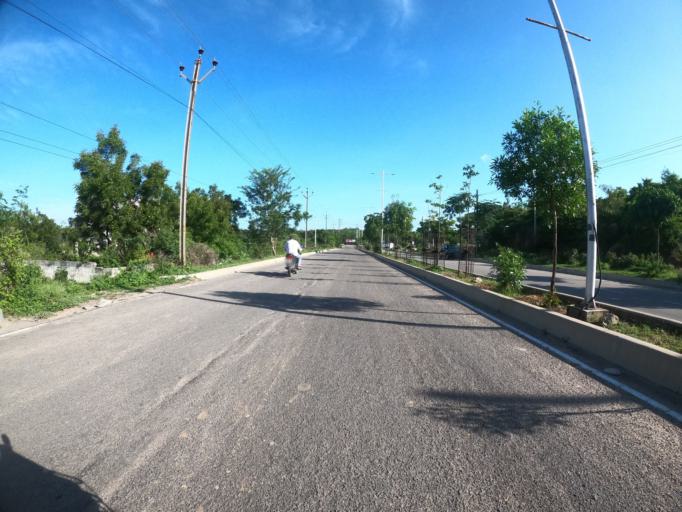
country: IN
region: Telangana
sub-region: Hyderabad
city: Hyderabad
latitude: 17.3524
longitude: 78.3698
